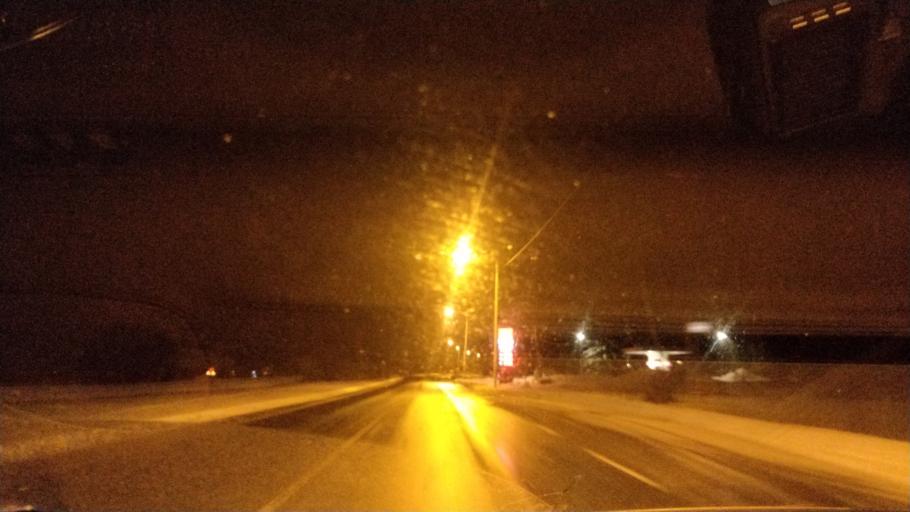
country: FI
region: Lapland
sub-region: Kemi-Tornio
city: Tervola
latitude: 66.1452
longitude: 24.9625
